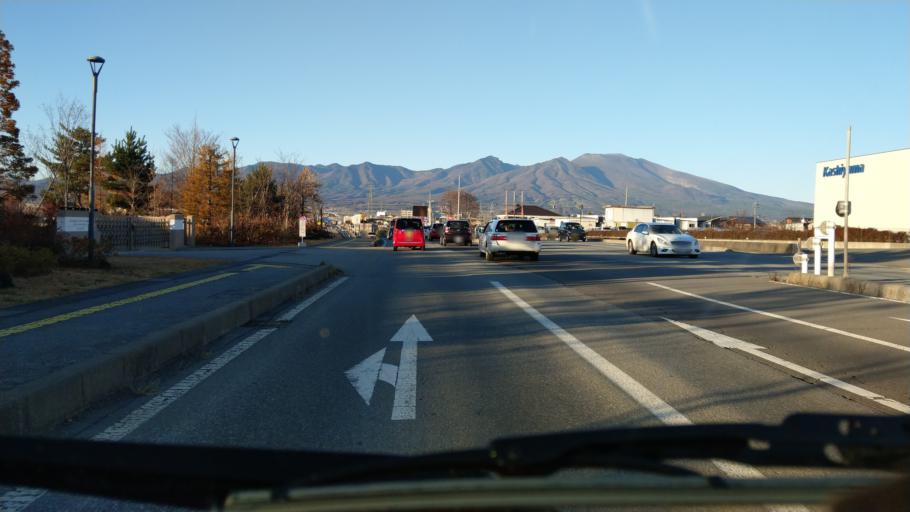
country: JP
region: Nagano
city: Saku
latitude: 36.2579
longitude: 138.4678
